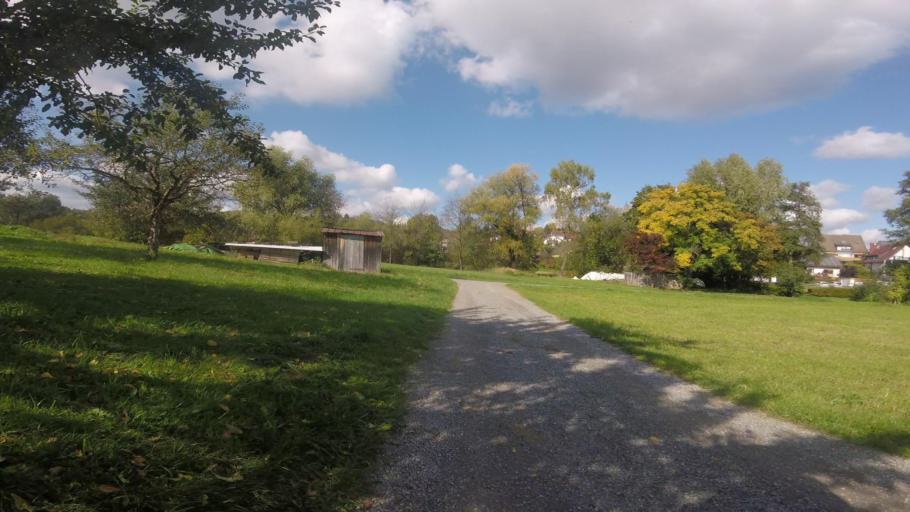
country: DE
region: Baden-Wuerttemberg
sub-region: Regierungsbezirk Stuttgart
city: Oberstenfeld
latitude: 48.9909
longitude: 9.3553
